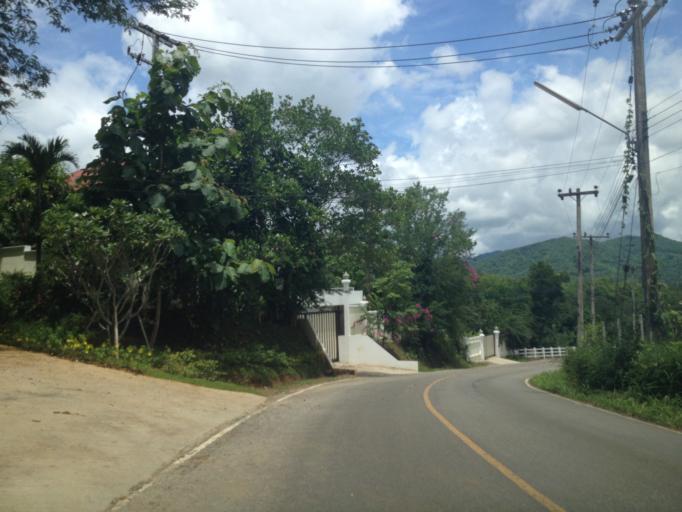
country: TH
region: Chiang Mai
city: Hang Dong
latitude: 18.7174
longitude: 98.8870
